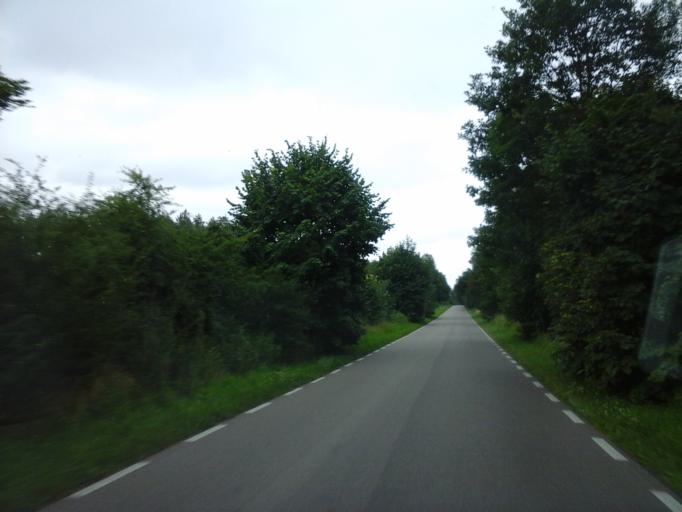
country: PL
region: West Pomeranian Voivodeship
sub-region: Powiat choszczenski
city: Pelczyce
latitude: 53.0914
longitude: 15.2715
